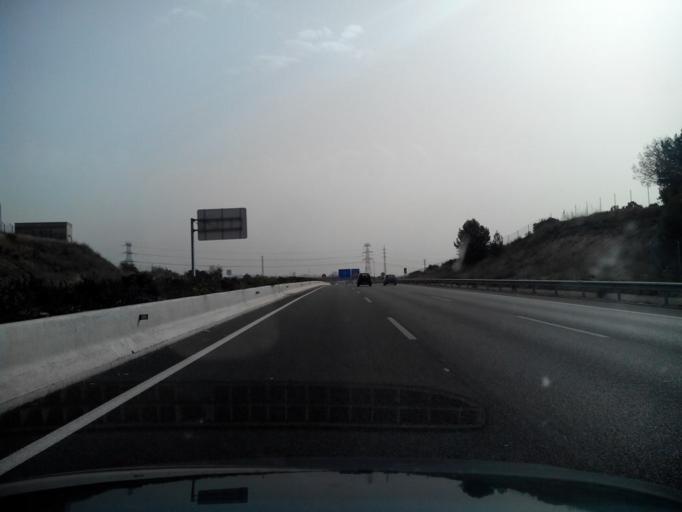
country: ES
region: Catalonia
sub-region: Provincia de Tarragona
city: Constanti
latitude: 41.1315
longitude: 1.1893
